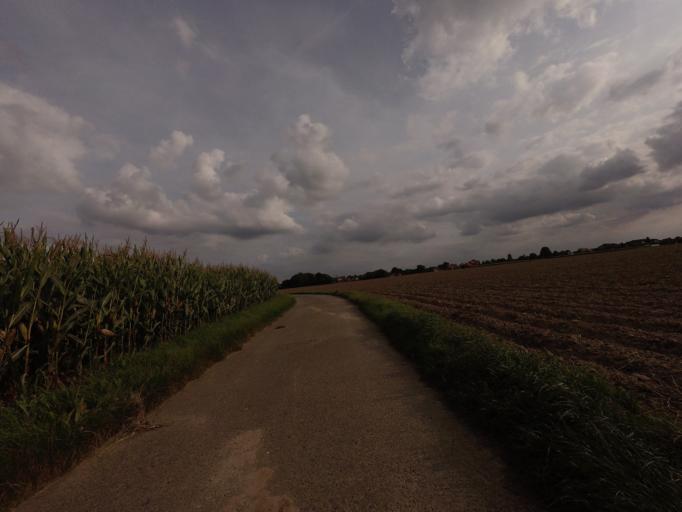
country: BE
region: Flanders
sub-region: Provincie Vlaams-Brabant
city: Kampenhout
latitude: 50.9291
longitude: 4.5602
